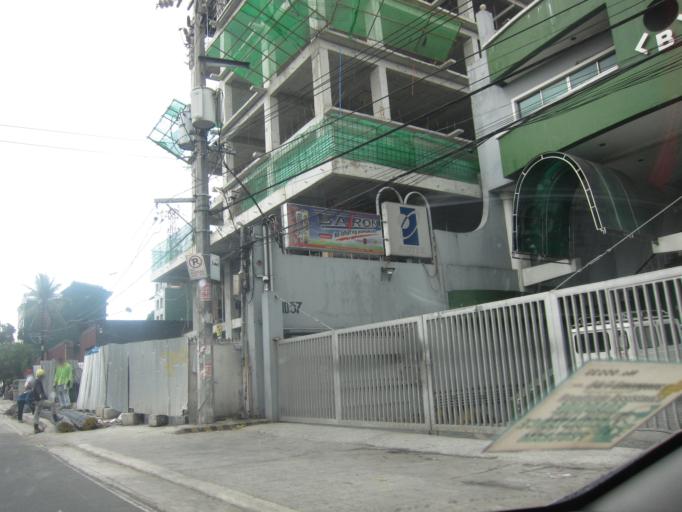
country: PH
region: Metro Manila
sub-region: Quezon City
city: Quezon City
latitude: 14.6390
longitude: 121.0548
